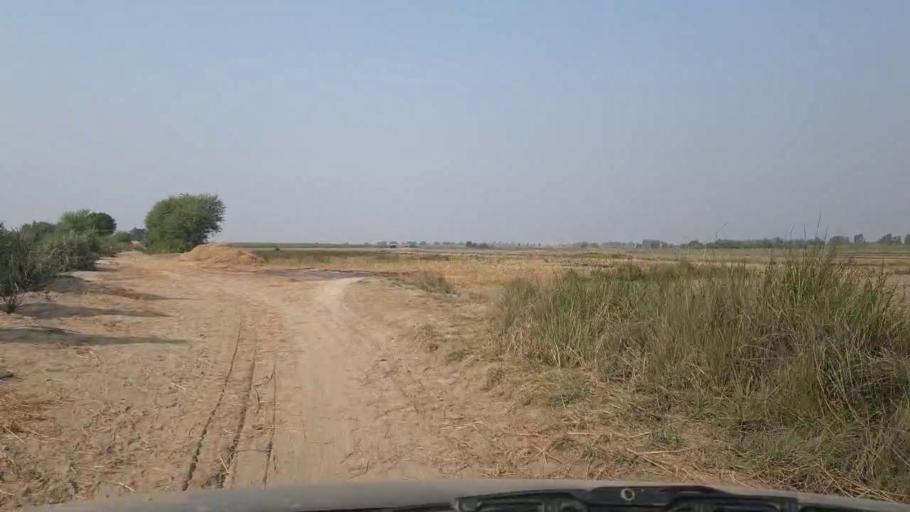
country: PK
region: Sindh
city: Tando Muhammad Khan
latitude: 25.0598
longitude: 68.3626
